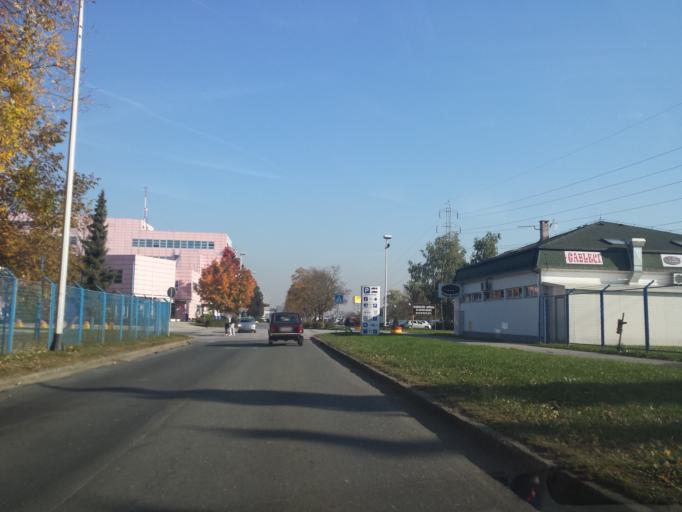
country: HR
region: Grad Zagreb
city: Stenjevec
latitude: 45.7989
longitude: 15.8753
